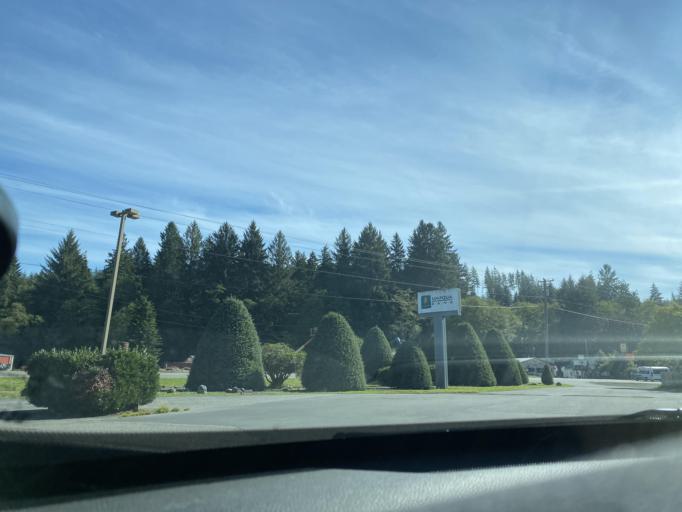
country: US
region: Washington
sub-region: Clallam County
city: Forks
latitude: 47.9410
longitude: -124.3864
